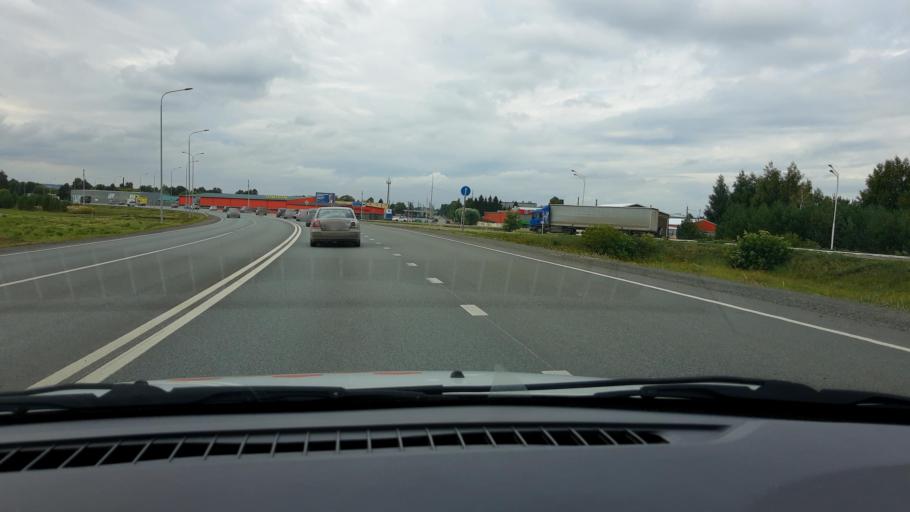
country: RU
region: Tatarstan
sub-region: Alekseyevskiy Rayon
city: Alekseyevskoye
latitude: 55.3078
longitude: 50.1390
